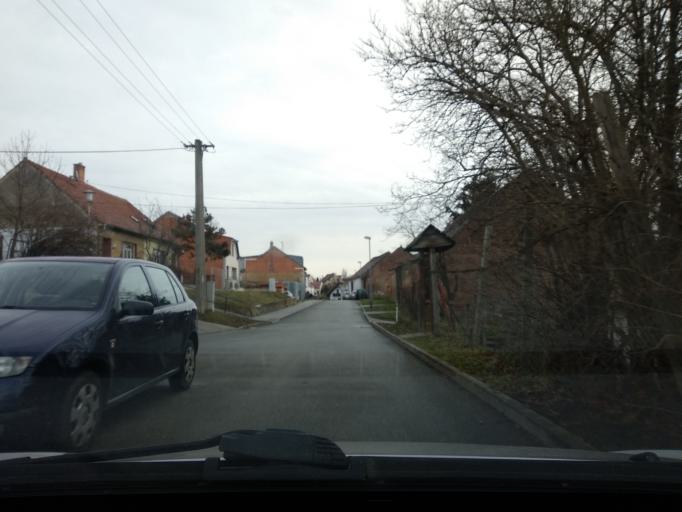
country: CZ
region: South Moravian
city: Ostopovice
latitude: 49.1656
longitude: 16.5621
